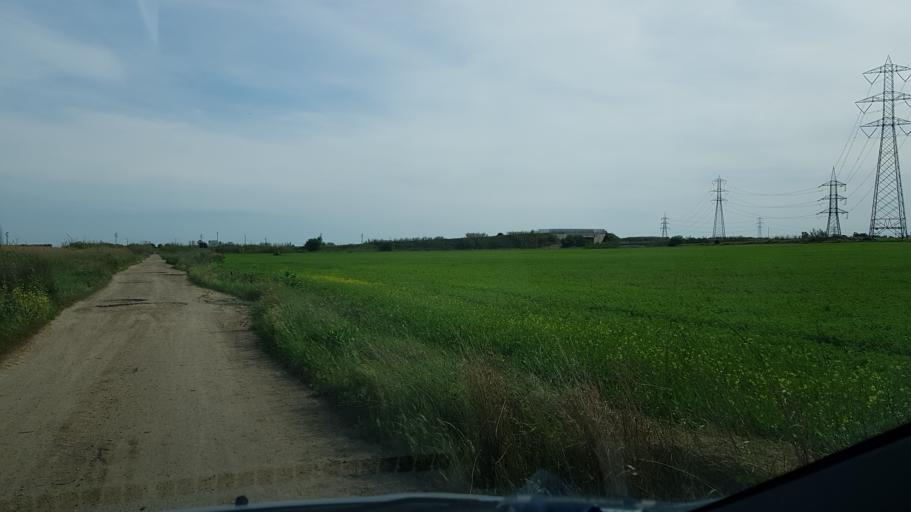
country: IT
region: Apulia
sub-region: Provincia di Brindisi
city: La Rosa
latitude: 40.6031
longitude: 17.9698
